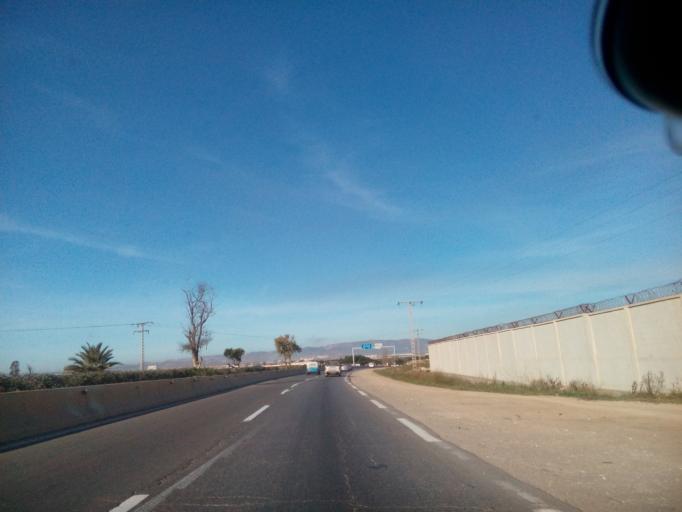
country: DZ
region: Oran
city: Ain el Bya
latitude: 35.7815
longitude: -0.2805
